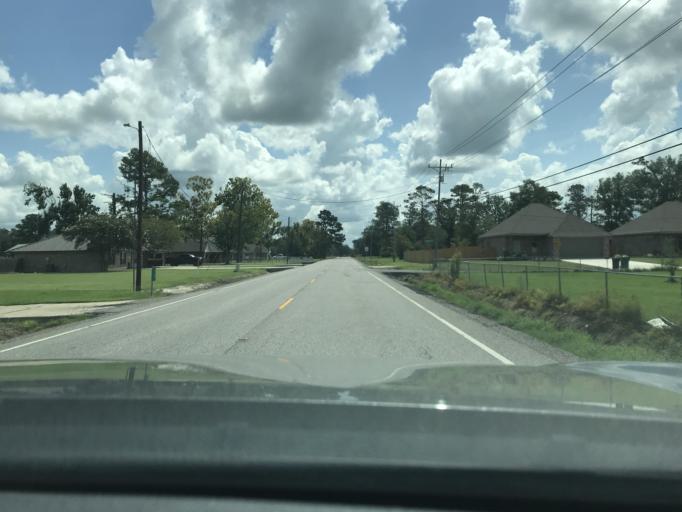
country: US
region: Louisiana
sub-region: Calcasieu Parish
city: Moss Bluff
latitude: 30.3447
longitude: -93.2192
